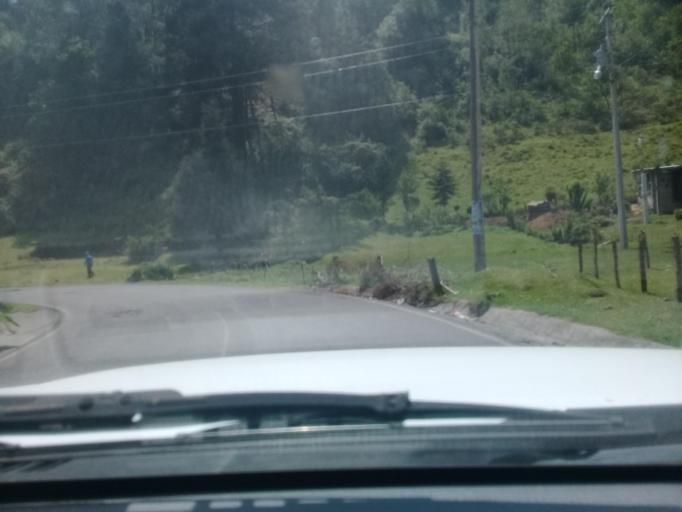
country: MX
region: Veracruz
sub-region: Mariano Escobedo
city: Texmola
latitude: 18.9456
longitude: -97.2218
